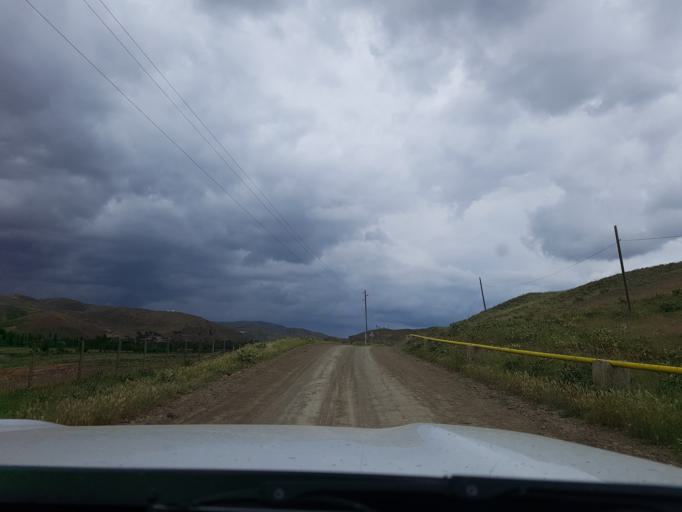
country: TM
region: Ahal
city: Baharly
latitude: 38.2156
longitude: 56.9882
